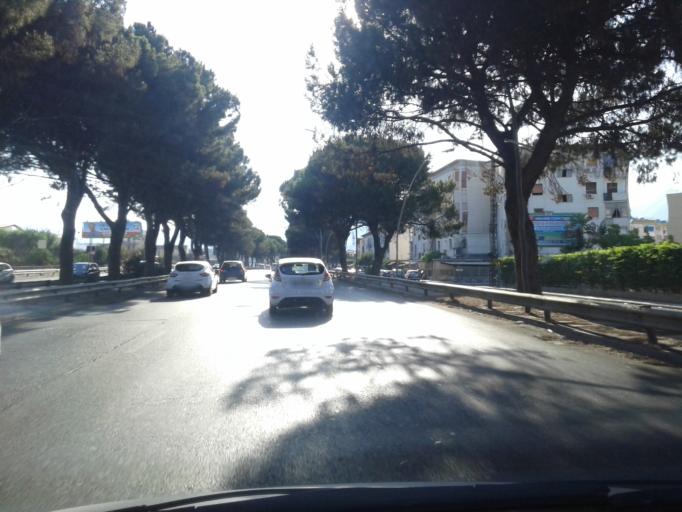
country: IT
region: Sicily
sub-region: Palermo
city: Villa Ciambra
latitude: 38.0868
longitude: 13.3555
